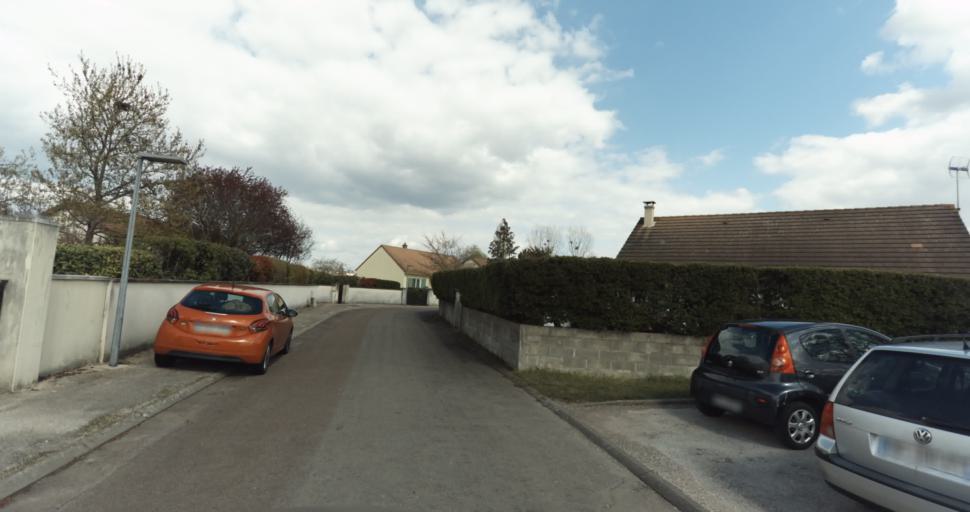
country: FR
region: Bourgogne
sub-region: Departement de la Cote-d'Or
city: Auxonne
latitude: 47.1908
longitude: 5.4028
